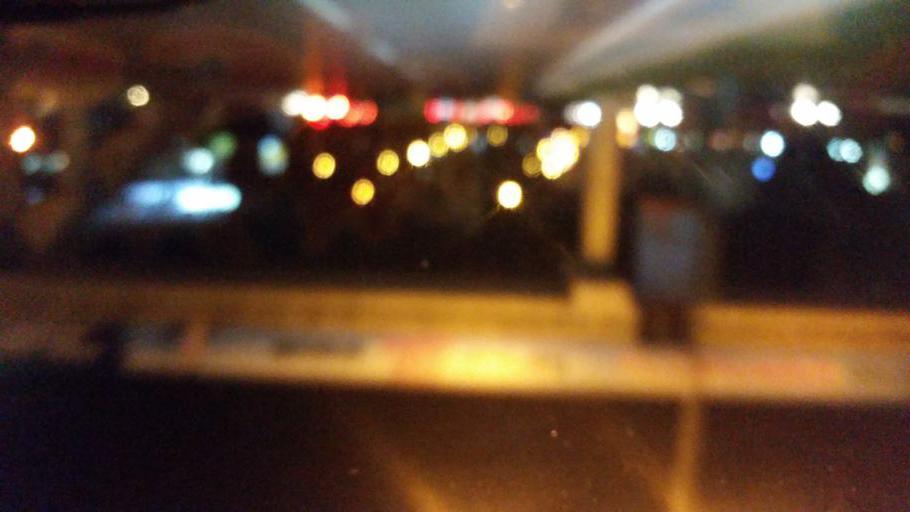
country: TR
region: Istanbul
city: Gurpinar
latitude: 41.0252
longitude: 28.6285
